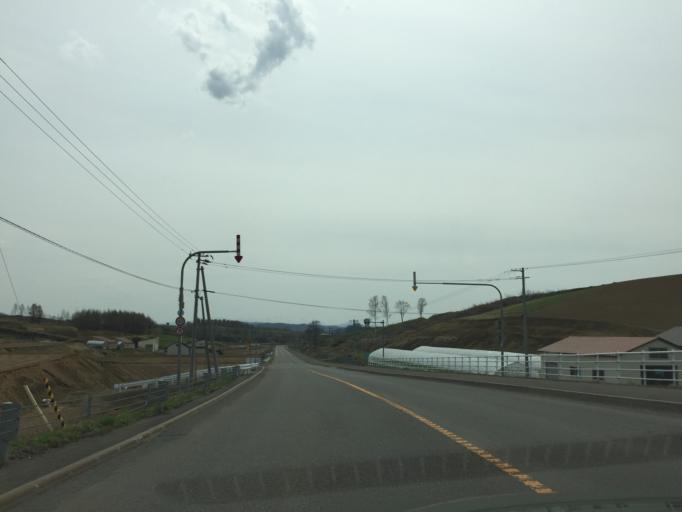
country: JP
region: Hokkaido
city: Ashibetsu
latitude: 43.6332
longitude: 142.1982
